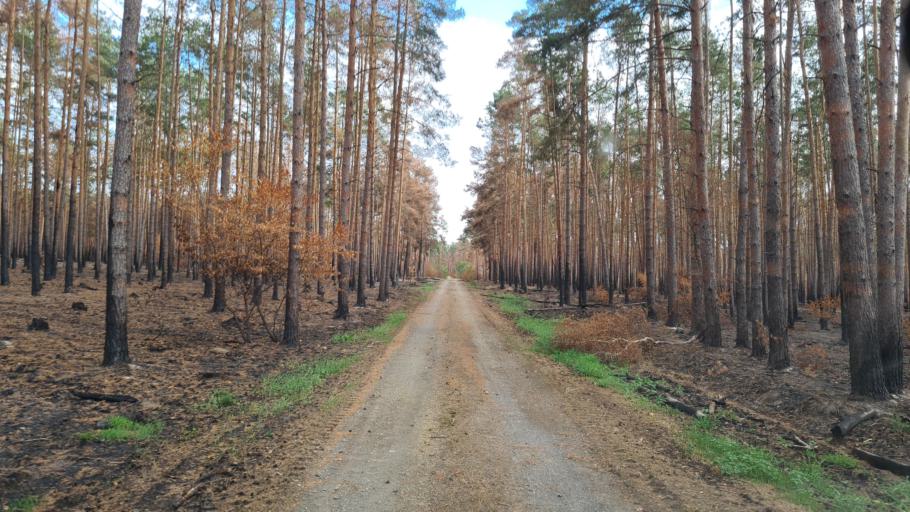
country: DE
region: Saxony
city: Arzberg
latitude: 51.5612
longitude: 13.1841
